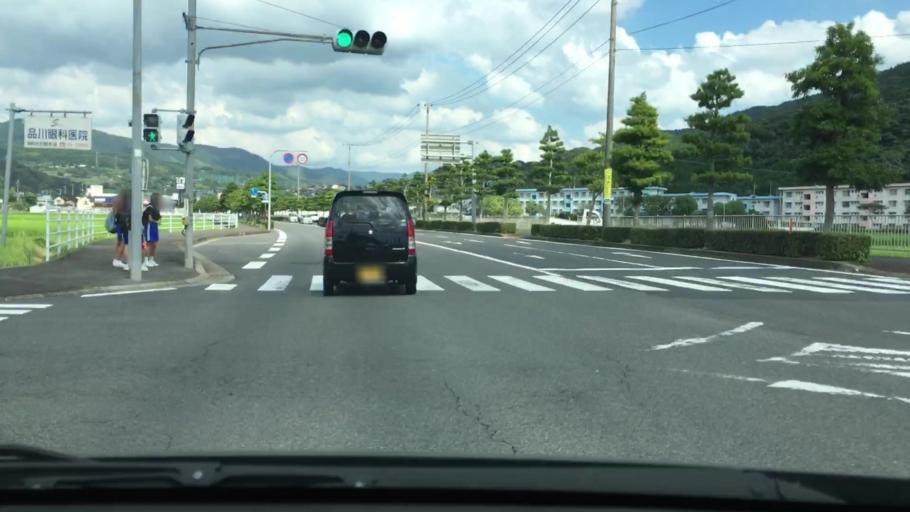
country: JP
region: Nagasaki
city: Sasebo
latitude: 33.2064
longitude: 129.6874
